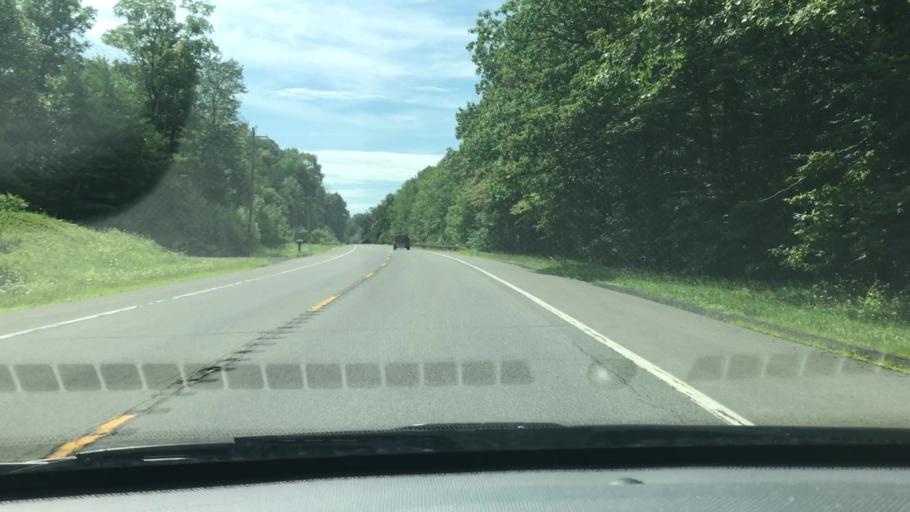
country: US
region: New York
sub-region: Ulster County
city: Shokan
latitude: 41.9876
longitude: -74.2606
